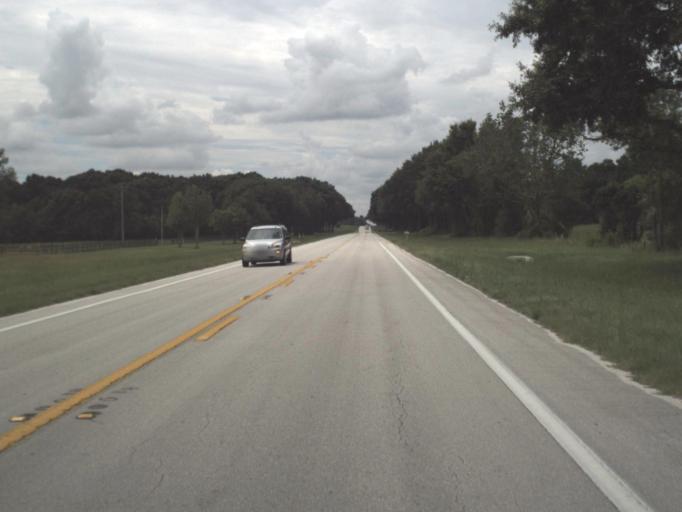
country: US
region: Florida
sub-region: Alachua County
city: High Springs
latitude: 29.7525
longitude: -82.6074
